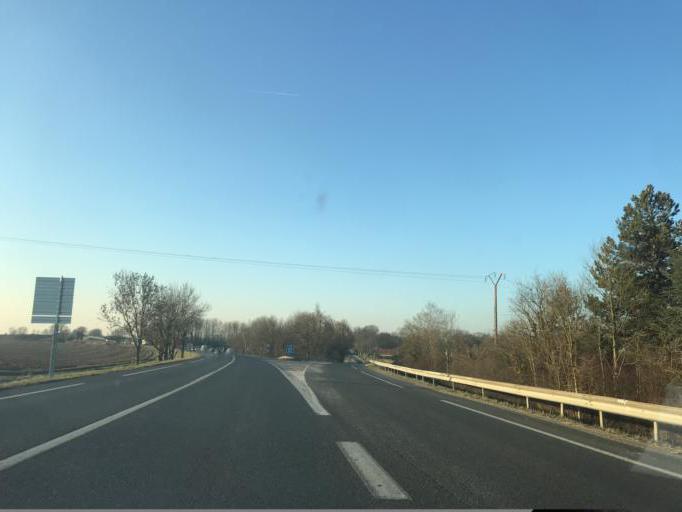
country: FR
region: Ile-de-France
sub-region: Departement de Seine-et-Marne
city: Villiers-sur-Morin
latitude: 48.8520
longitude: 2.8629
